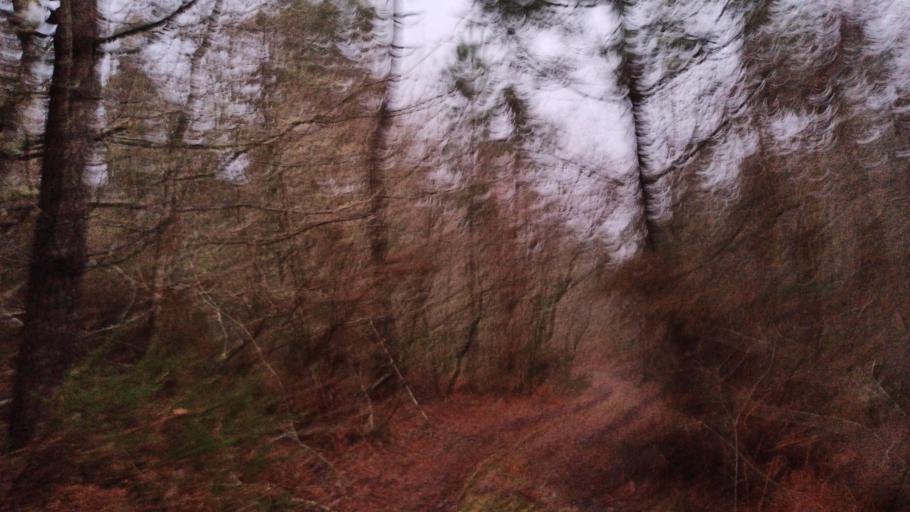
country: ES
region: Galicia
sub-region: Provincia da Coruna
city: Negreira
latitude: 42.9082
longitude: -8.7687
